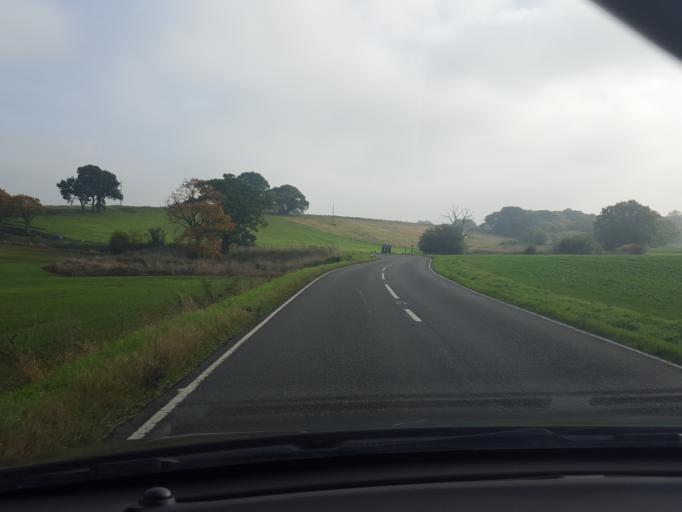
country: GB
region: England
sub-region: Essex
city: Mistley
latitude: 51.9391
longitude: 1.1067
